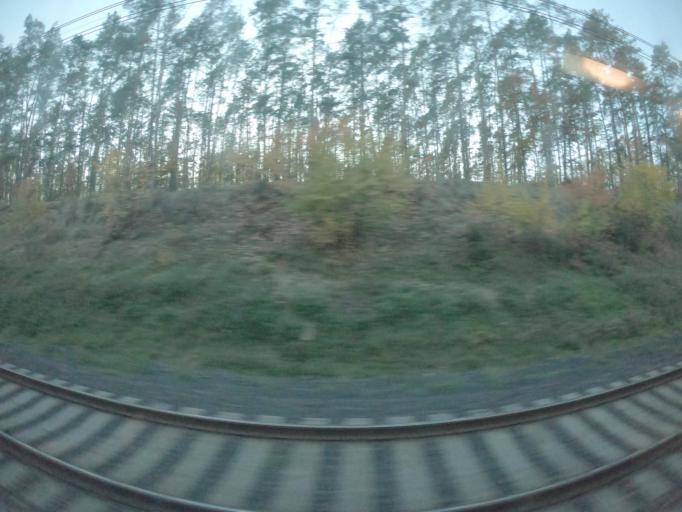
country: PL
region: West Pomeranian Voivodeship
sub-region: Powiat mysliborski
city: Boleszkowice
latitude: 52.7187
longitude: 14.5301
